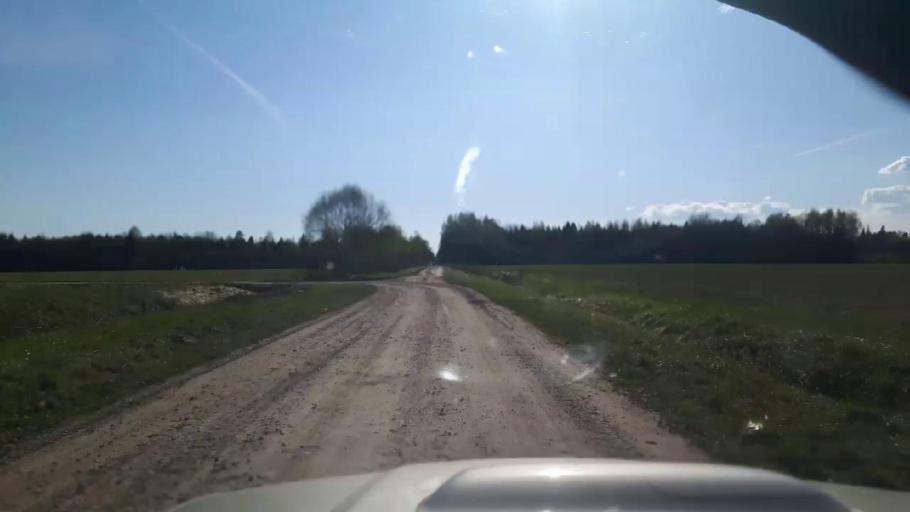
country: EE
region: Paernumaa
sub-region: Tootsi vald
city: Tootsi
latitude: 58.4343
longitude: 24.8503
